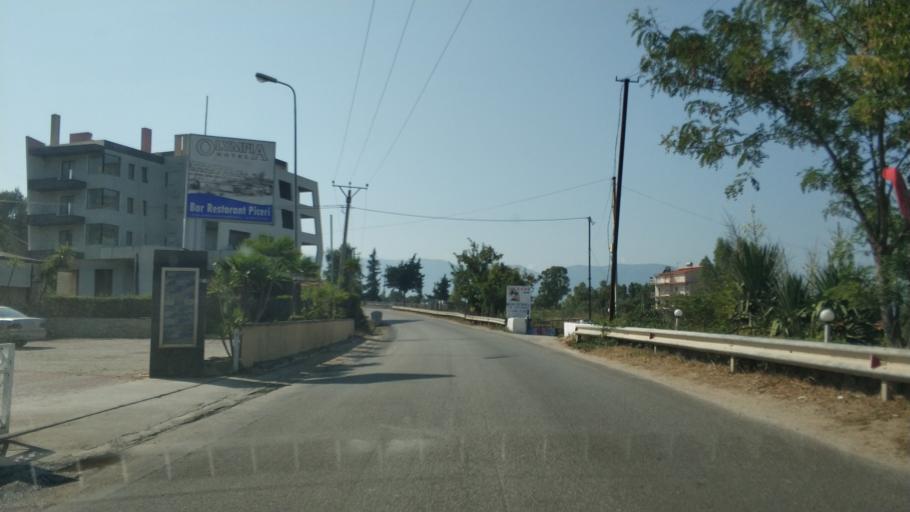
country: AL
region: Vlore
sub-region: Rrethi i Vlores
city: Orikum
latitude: 40.3787
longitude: 19.4813
